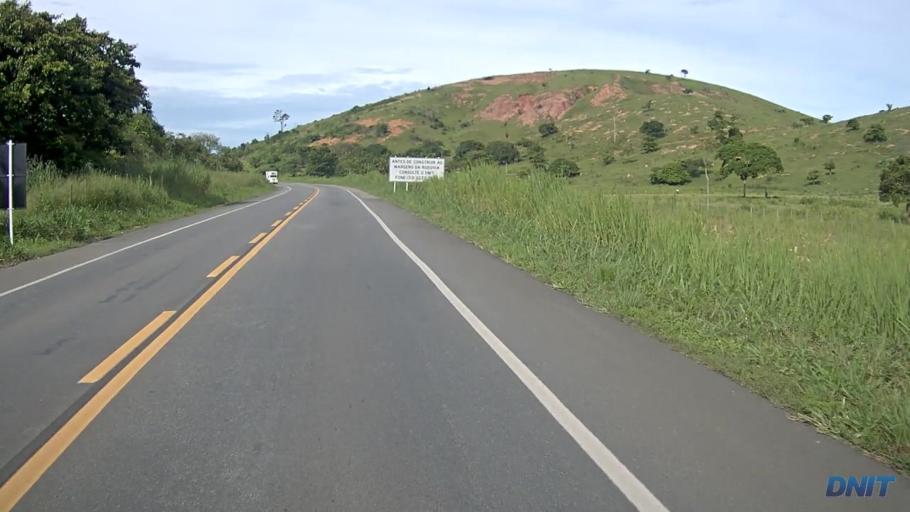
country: BR
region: Minas Gerais
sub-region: Belo Oriente
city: Belo Oriente
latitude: -19.2027
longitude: -42.2911
